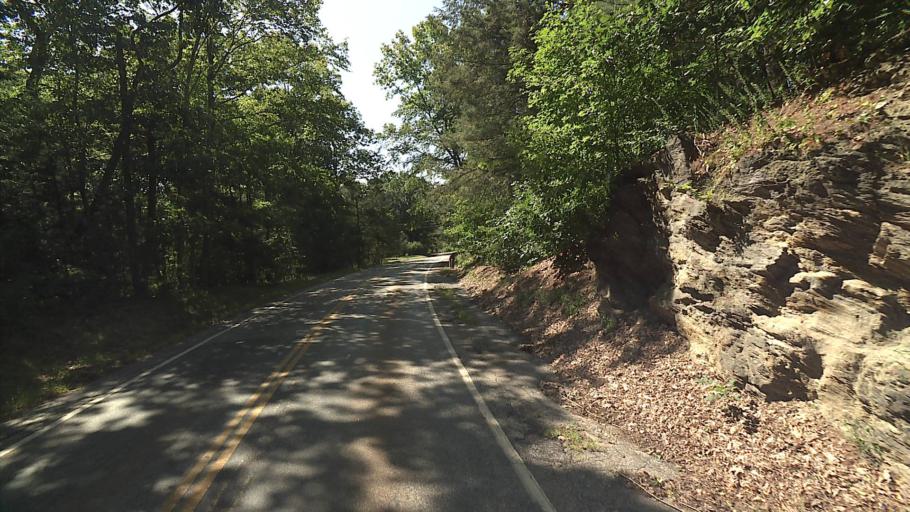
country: US
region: Connecticut
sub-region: Litchfield County
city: Thomaston
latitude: 41.7166
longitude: -73.0697
